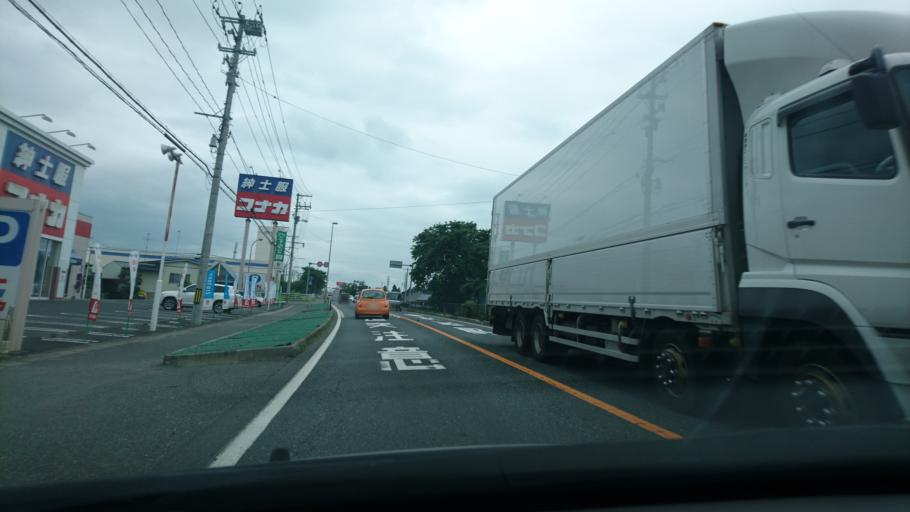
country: JP
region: Miyagi
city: Furukawa
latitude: 38.7437
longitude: 141.0158
